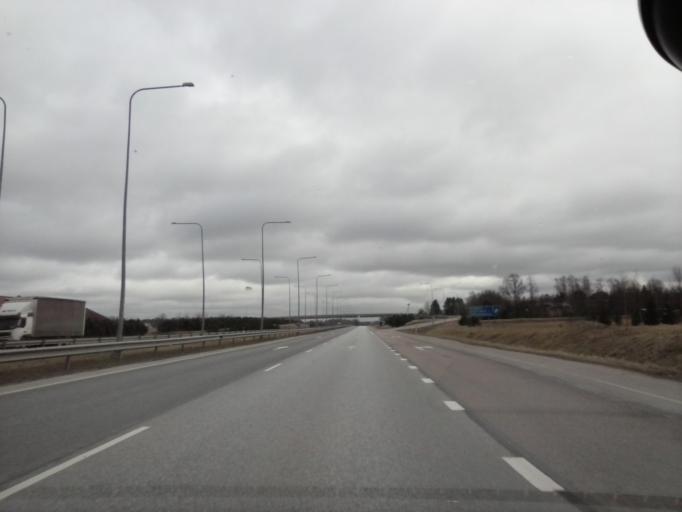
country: EE
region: Harju
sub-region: Rae vald
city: Vaida
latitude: 59.3162
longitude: 24.9309
